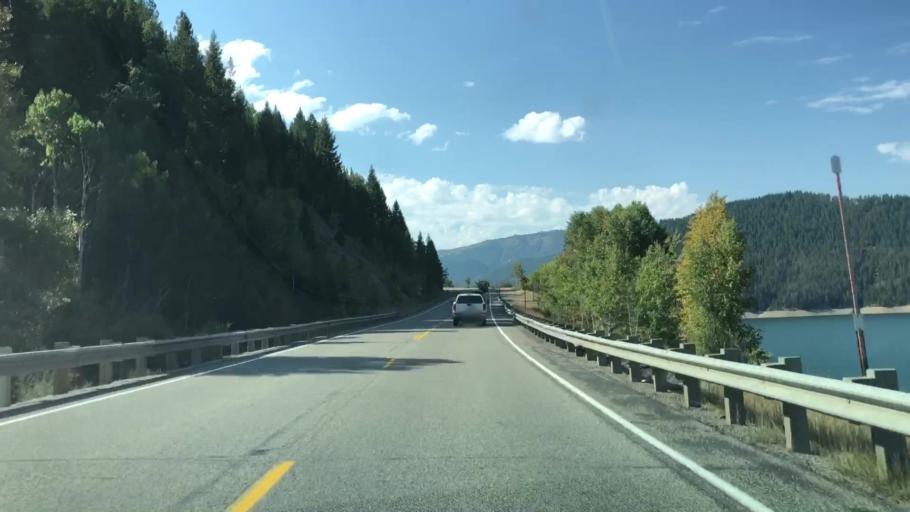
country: US
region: Idaho
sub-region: Teton County
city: Victor
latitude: 43.3173
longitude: -111.1450
